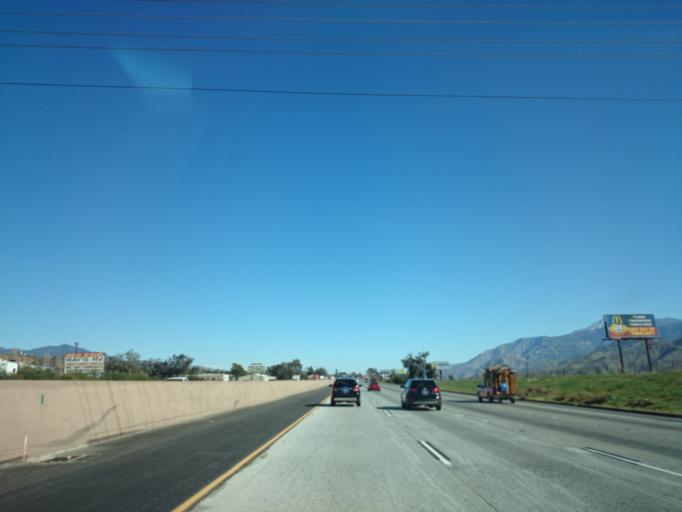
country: US
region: California
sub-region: Riverside County
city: Beaumont
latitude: 33.9262
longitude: -116.9286
